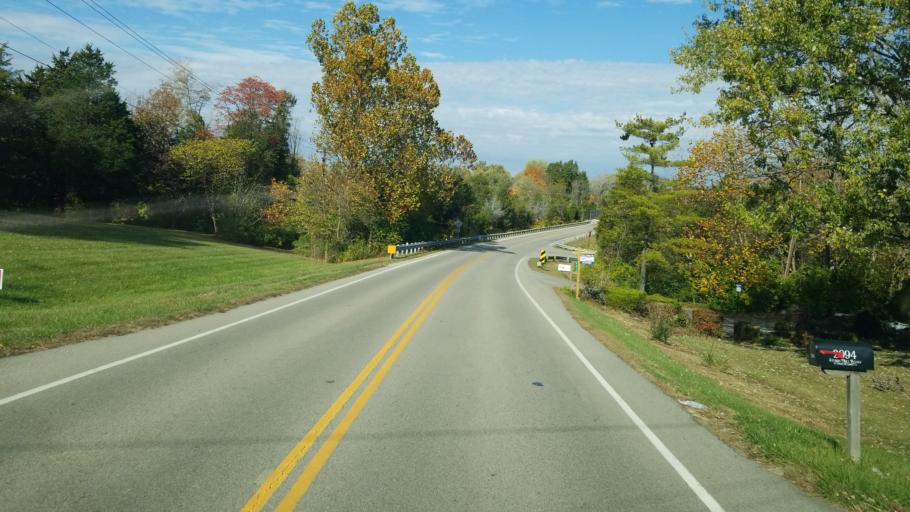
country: US
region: Ohio
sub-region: Warren County
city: Lebanon
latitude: 39.4009
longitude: -84.1760
